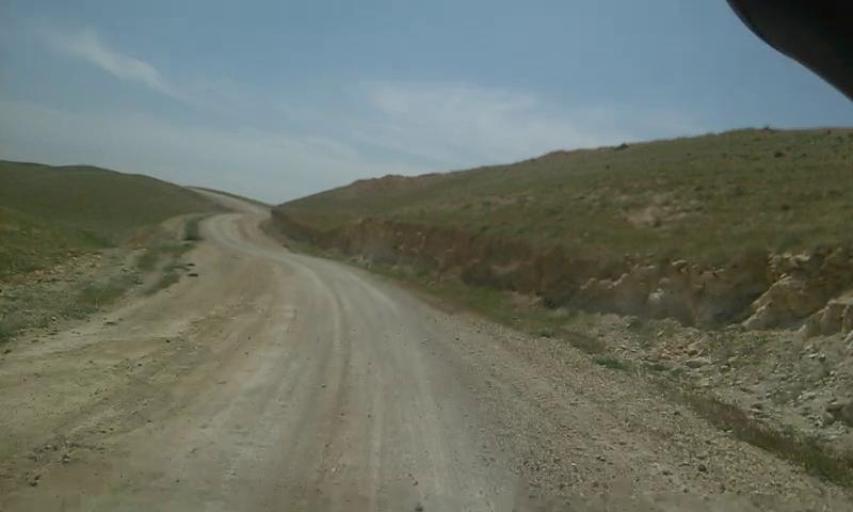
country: PS
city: `Arab ar Rashaydah
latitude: 31.5012
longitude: 35.2938
